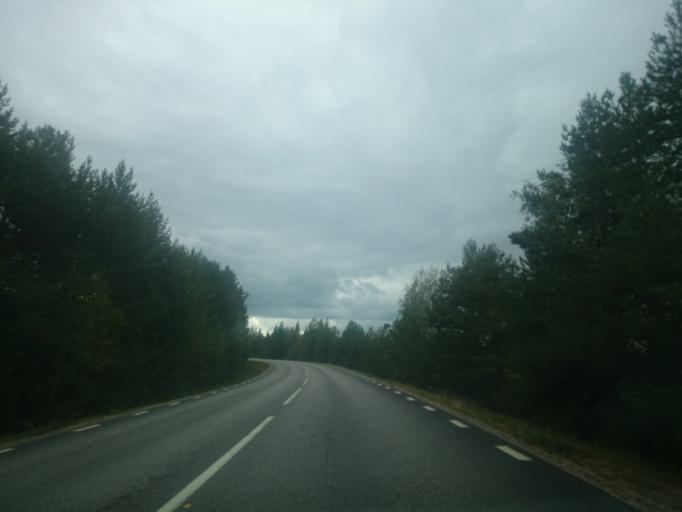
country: SE
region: Jaemtland
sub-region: Harjedalens Kommun
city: Sveg
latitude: 62.0430
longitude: 14.6412
